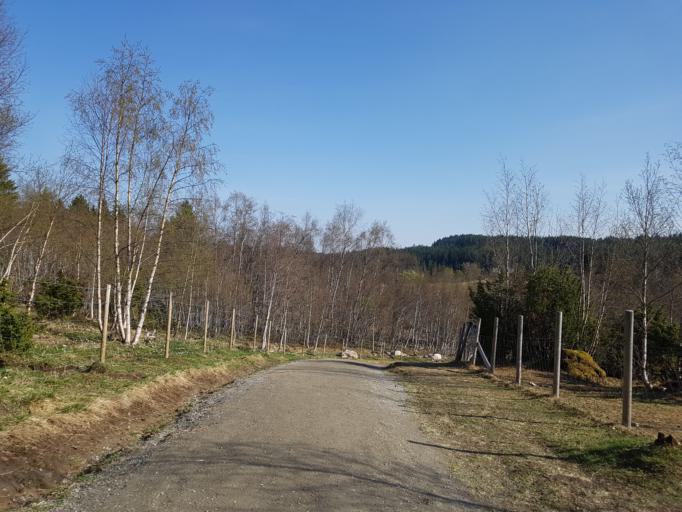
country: NO
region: Sor-Trondelag
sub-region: Trondheim
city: Trondheim
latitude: 63.4208
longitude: 10.3086
